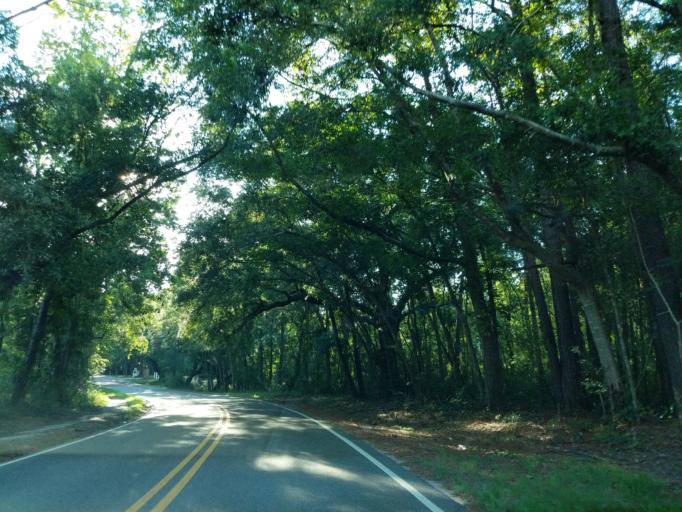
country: US
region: South Carolina
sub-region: Charleston County
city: Awendaw
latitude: 33.0938
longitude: -79.4679
